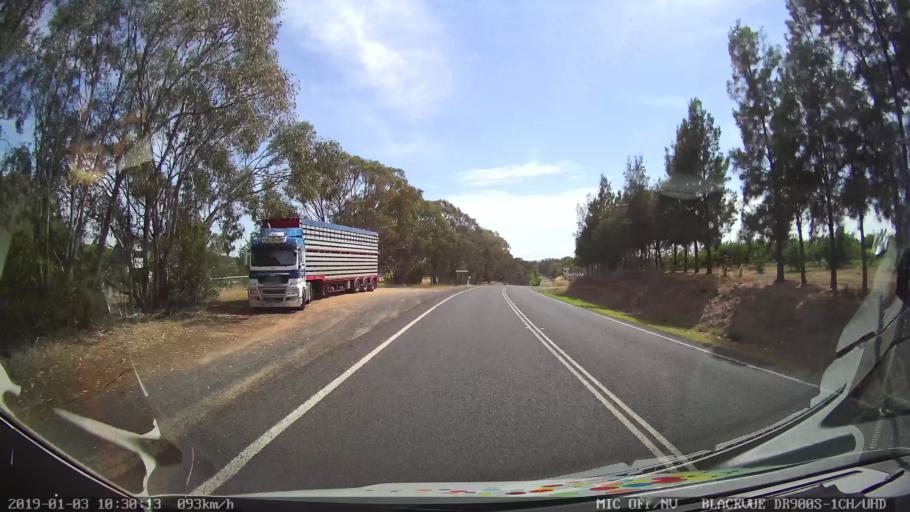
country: AU
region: New South Wales
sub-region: Young
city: Young
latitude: -34.3644
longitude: 148.2655
